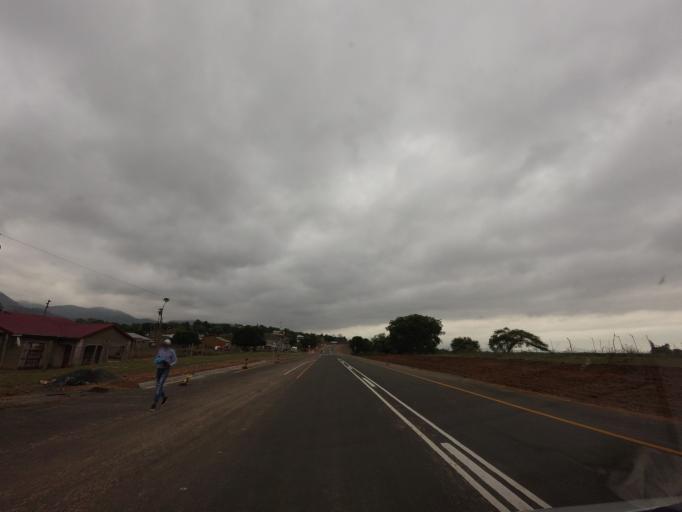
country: SZ
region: Hhohho
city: Ntfonjeni
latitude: -25.7327
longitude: 31.4796
